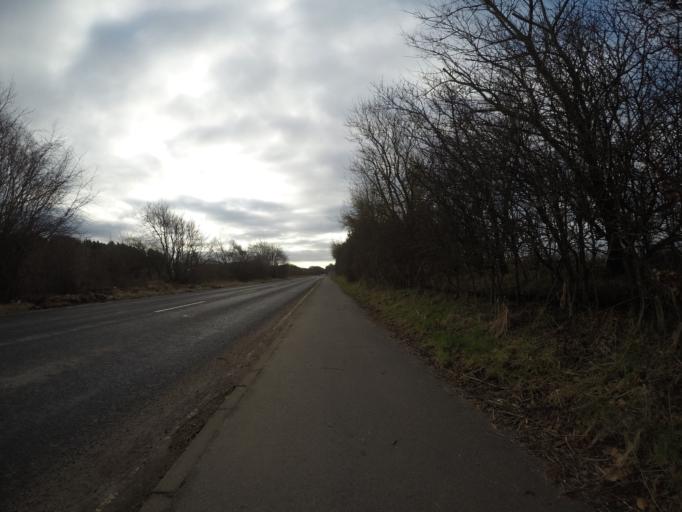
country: GB
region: Scotland
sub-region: North Ayrshire
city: Irvine
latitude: 55.5886
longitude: -4.6496
